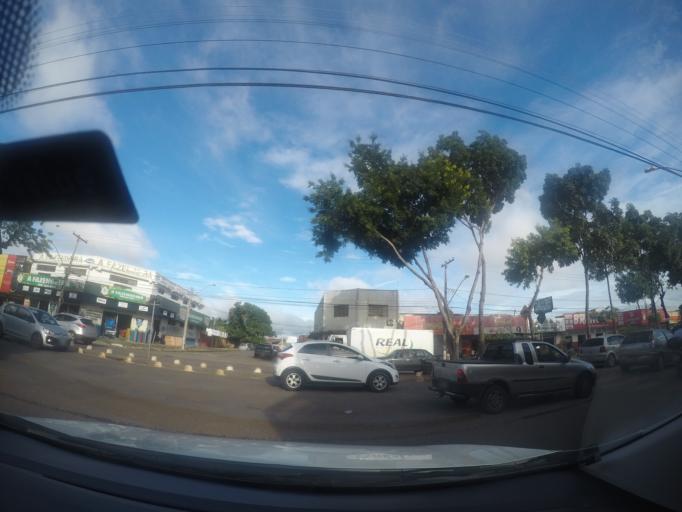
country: BR
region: Goias
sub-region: Goiania
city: Goiania
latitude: -16.6900
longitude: -49.3155
